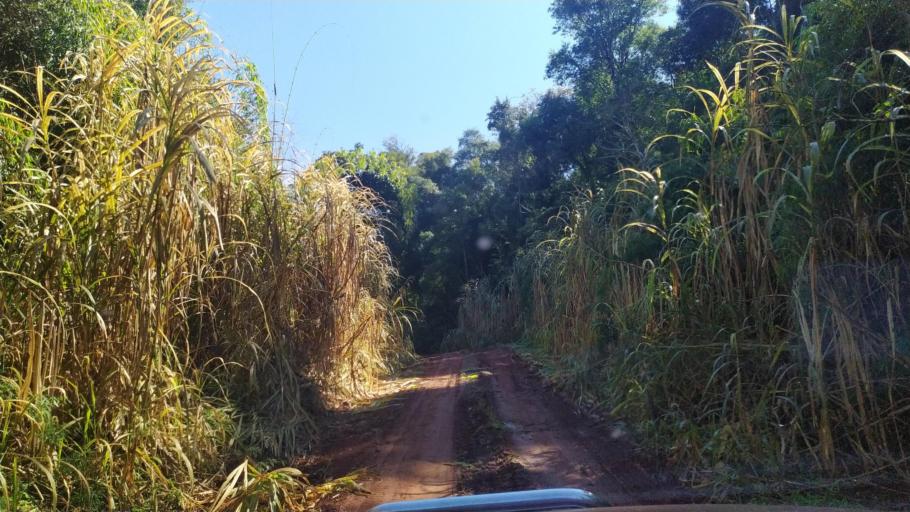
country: AR
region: Misiones
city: El Alcazar
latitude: -26.7547
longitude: -54.5983
